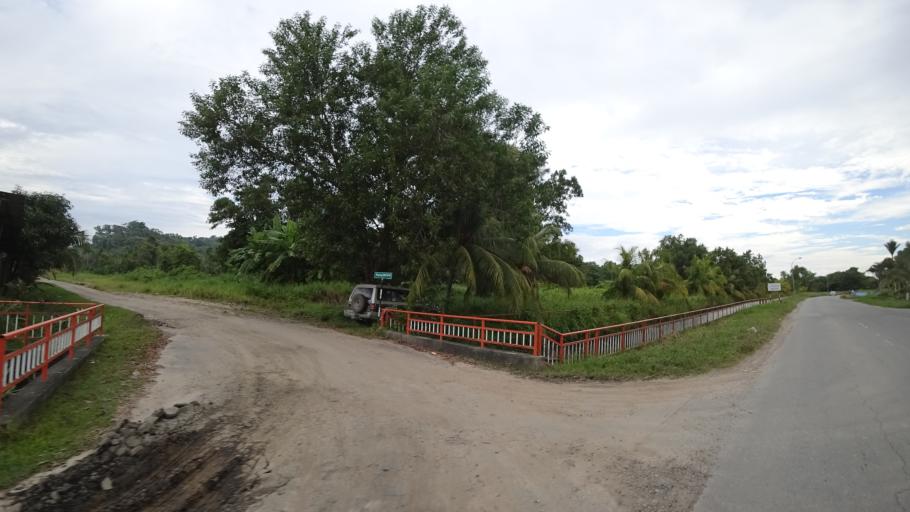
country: BN
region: Brunei and Muara
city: Bandar Seri Begawan
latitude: 4.8755
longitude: 114.8664
